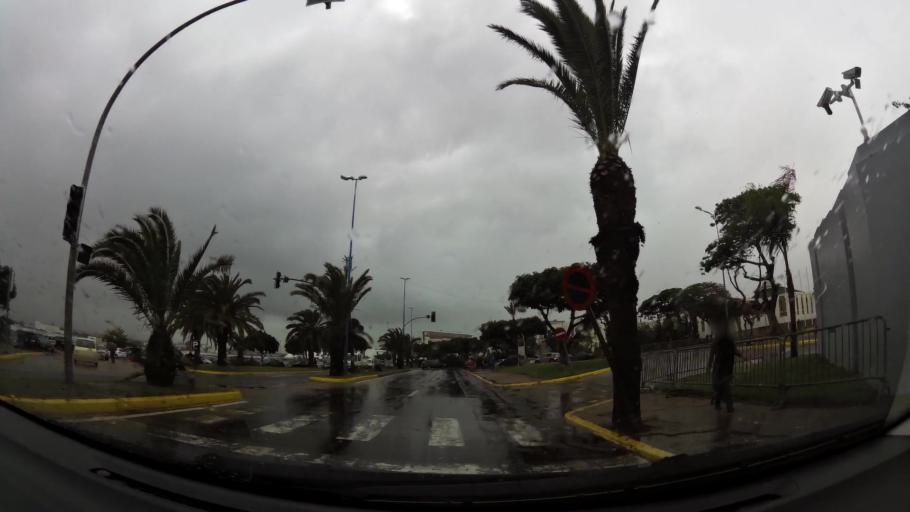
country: MA
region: Grand Casablanca
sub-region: Casablanca
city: Casablanca
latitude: 33.5555
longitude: -7.6668
